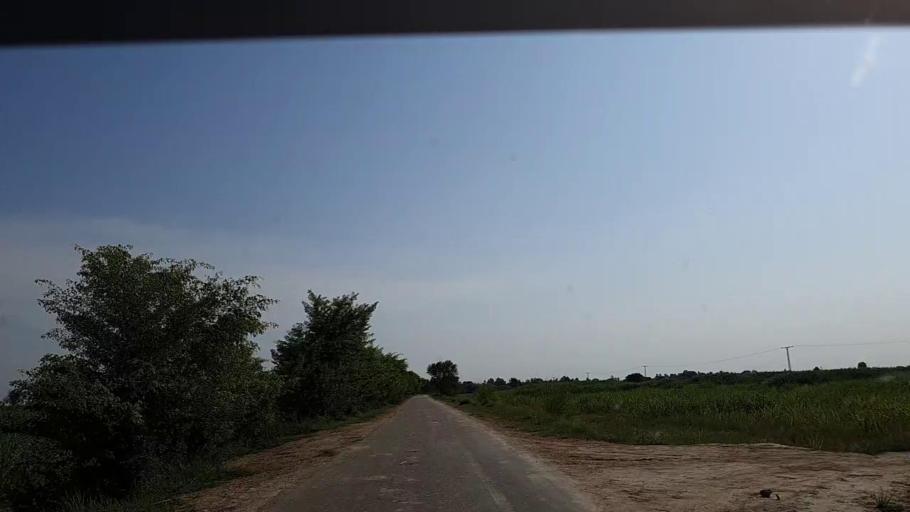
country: PK
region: Sindh
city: Adilpur
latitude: 27.9274
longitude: 69.2516
